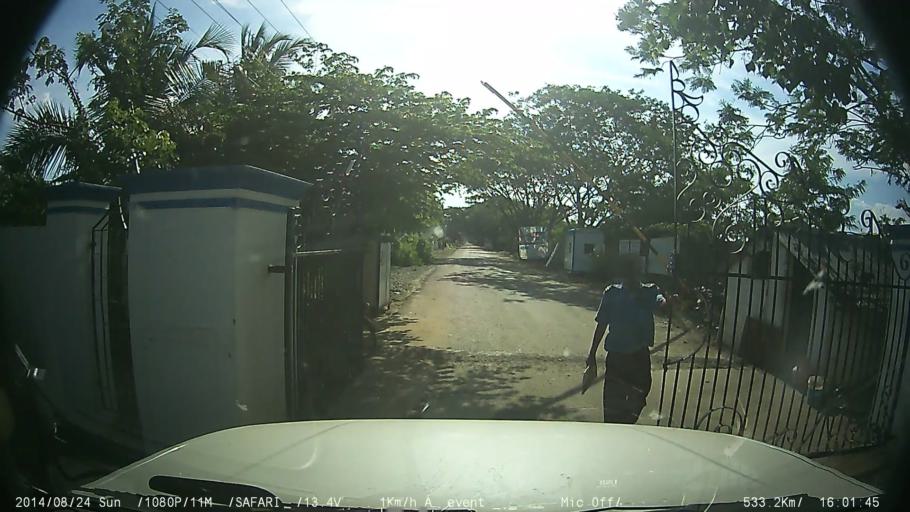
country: IN
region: Tamil Nadu
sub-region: Kancheepuram
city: Injambakkam
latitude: 12.8161
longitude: 80.2291
